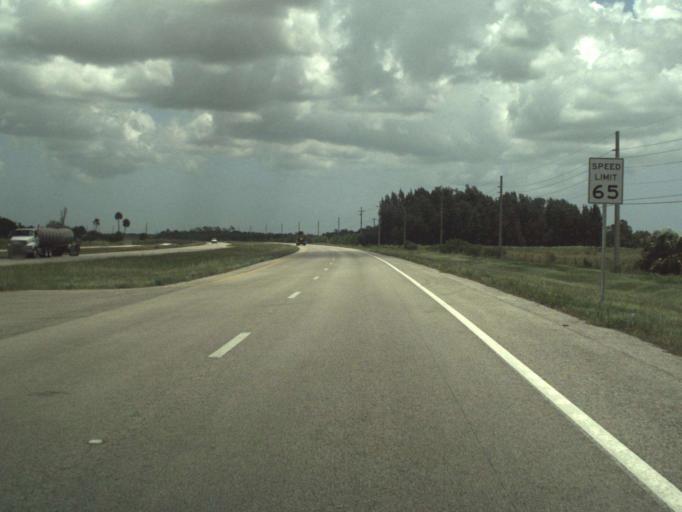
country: US
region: Florida
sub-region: Saint Lucie County
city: Fort Pierce South
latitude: 27.3869
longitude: -80.4643
